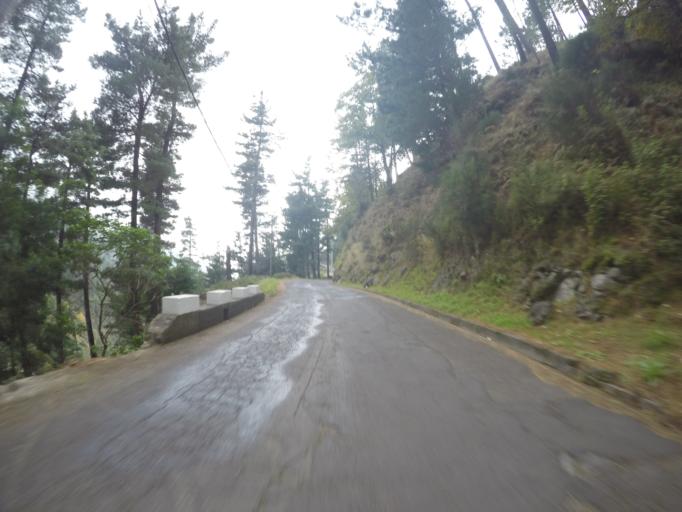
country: PT
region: Madeira
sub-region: Camara de Lobos
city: Curral das Freiras
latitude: 32.7037
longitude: -16.9548
